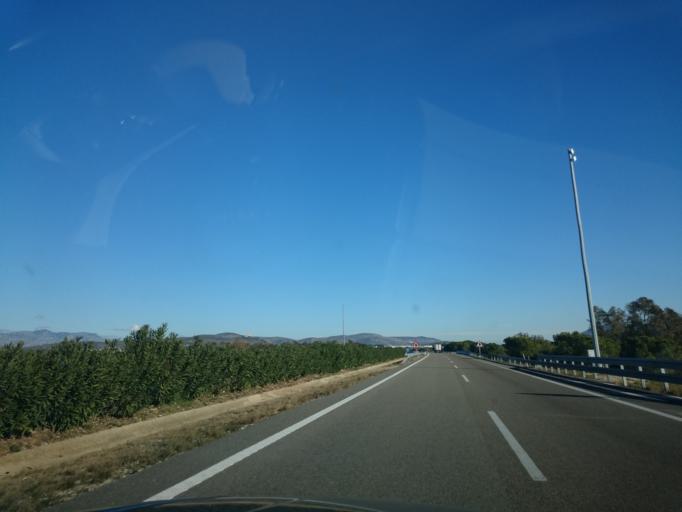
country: ES
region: Catalonia
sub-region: Provincia de Tarragona
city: Ulldecona
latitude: 40.5560
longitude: 0.4257
